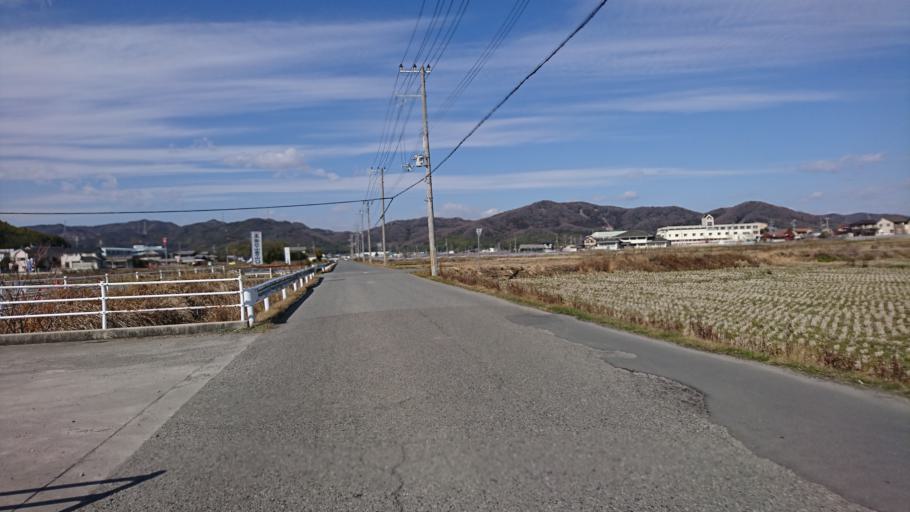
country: JP
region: Hyogo
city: Kakogawacho-honmachi
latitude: 34.8122
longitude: 134.8075
